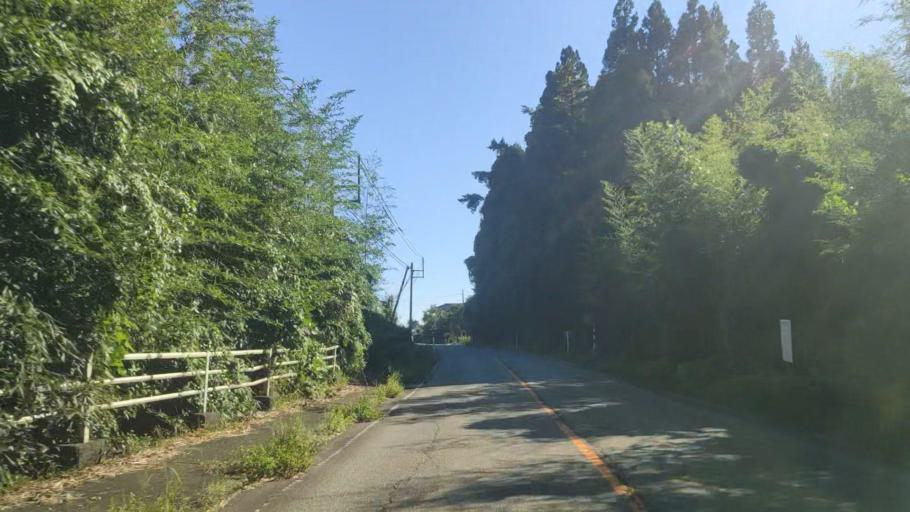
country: JP
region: Ishikawa
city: Nanao
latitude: 37.2614
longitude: 137.0889
